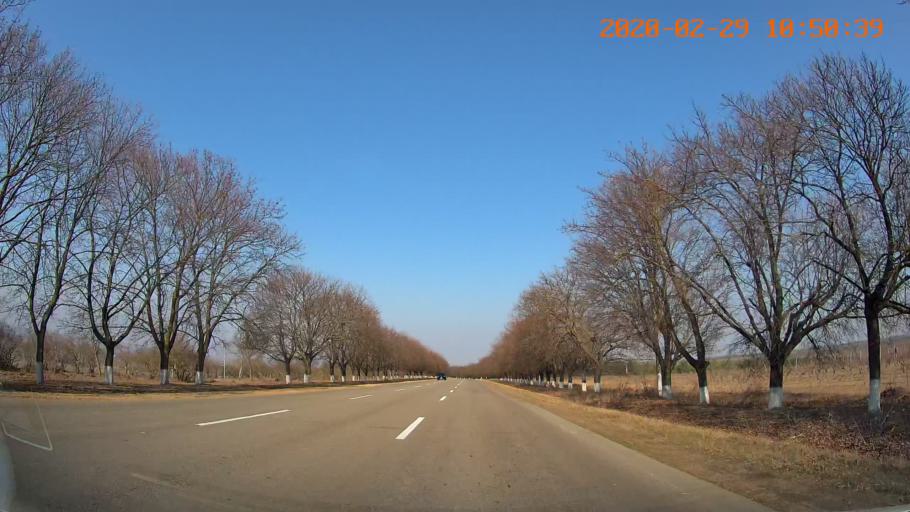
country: MD
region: Telenesti
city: Grigoriopol
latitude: 47.0853
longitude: 29.3731
